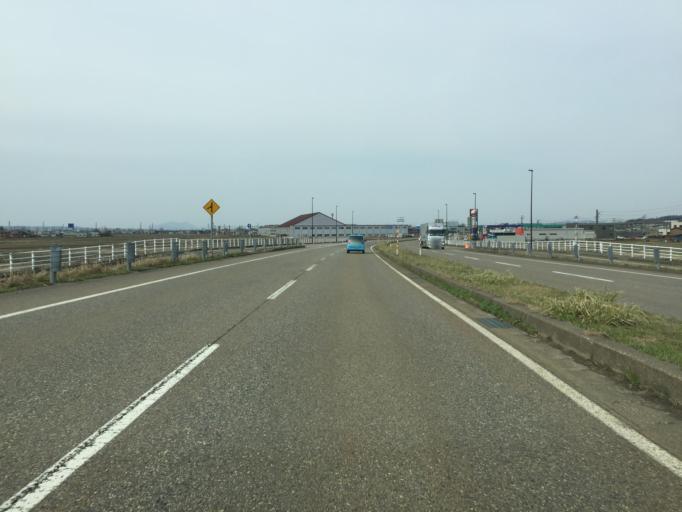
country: JP
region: Niigata
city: Nagaoka
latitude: 37.3930
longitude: 138.8369
